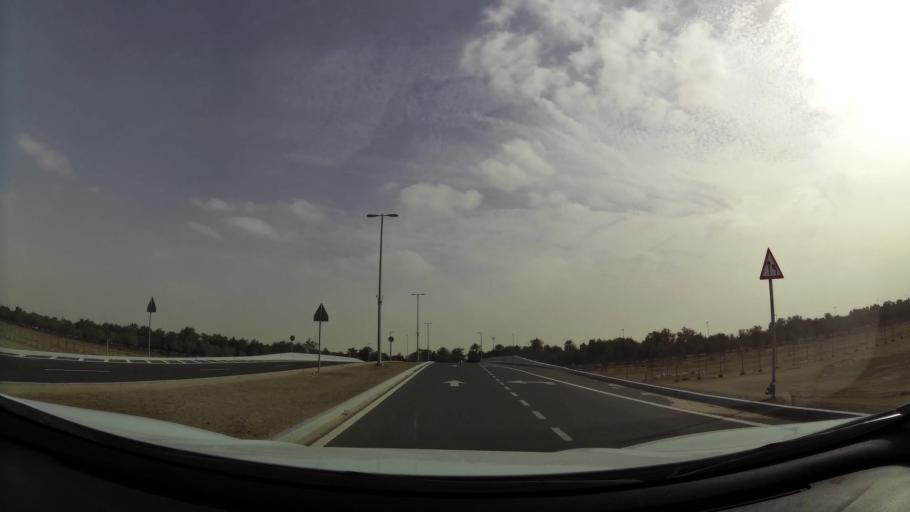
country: AE
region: Abu Dhabi
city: Abu Dhabi
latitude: 24.4027
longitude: 54.5895
